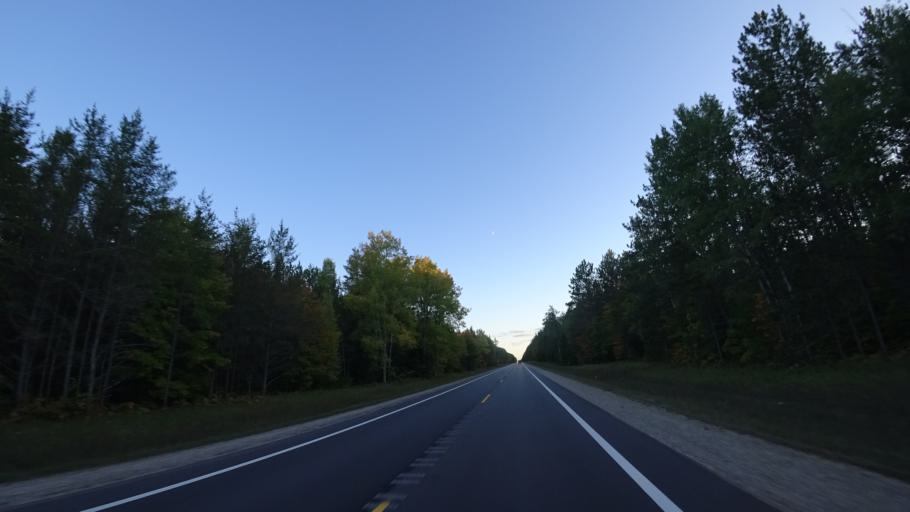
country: US
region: Michigan
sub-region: Luce County
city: Newberry
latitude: 46.3070
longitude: -85.0094
